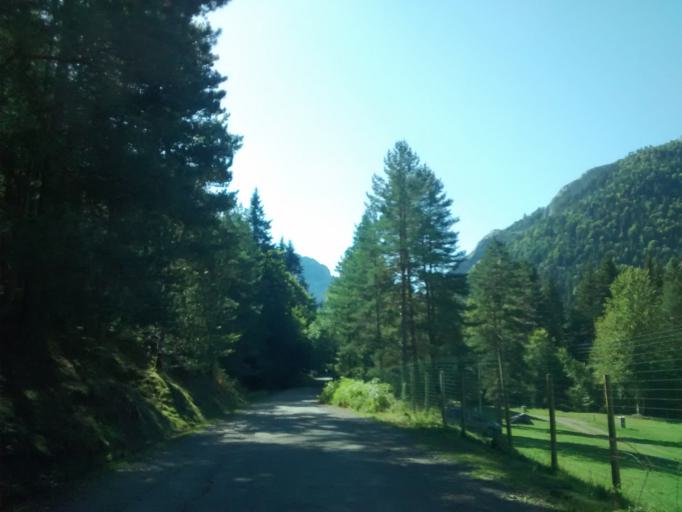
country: ES
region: Aragon
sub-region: Provincia de Huesca
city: Aragues del Puerto
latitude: 42.8364
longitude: -0.7111
